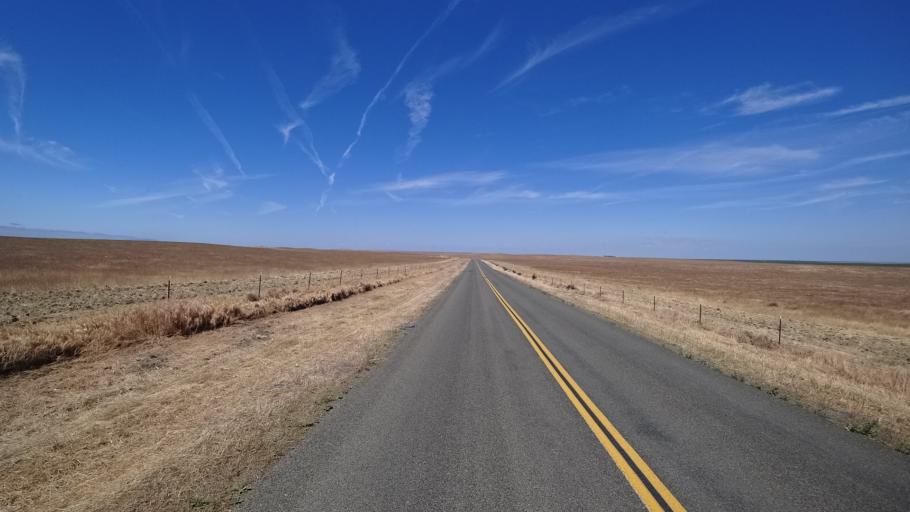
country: US
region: California
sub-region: Kings County
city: Kettleman City
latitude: 35.8060
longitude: -119.8978
